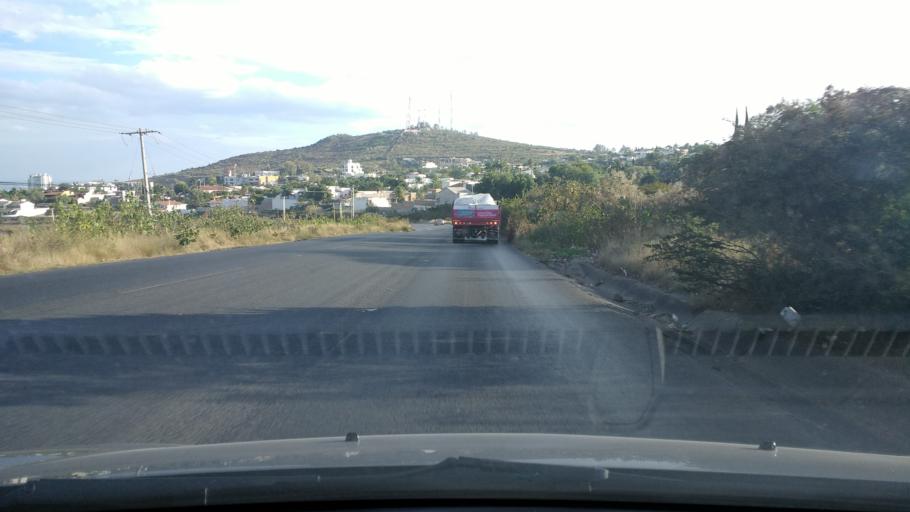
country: MX
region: Guanajuato
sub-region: Leon
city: La Ermita
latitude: 21.1746
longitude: -101.7227
